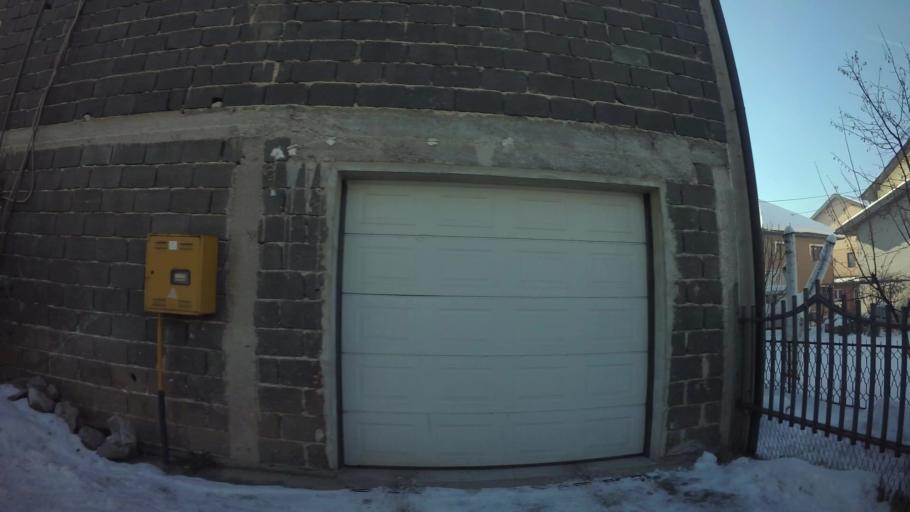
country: BA
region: Federation of Bosnia and Herzegovina
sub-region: Kanton Sarajevo
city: Sarajevo
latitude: 43.8083
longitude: 18.3153
